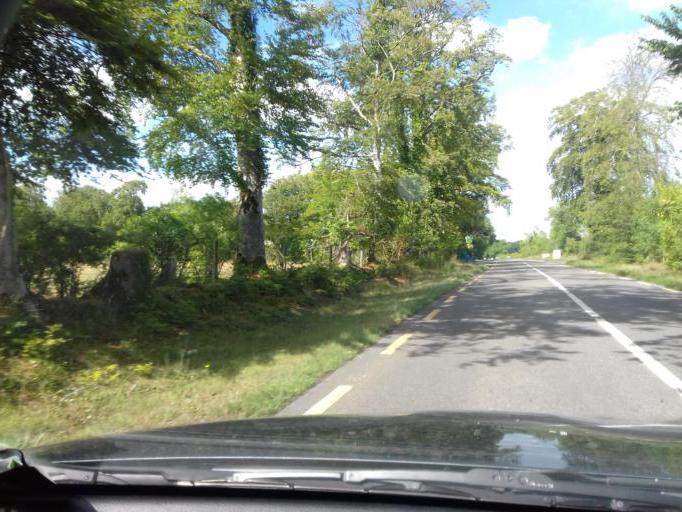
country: IE
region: Leinster
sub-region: Wicklow
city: Blessington
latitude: 53.1441
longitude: -6.5588
